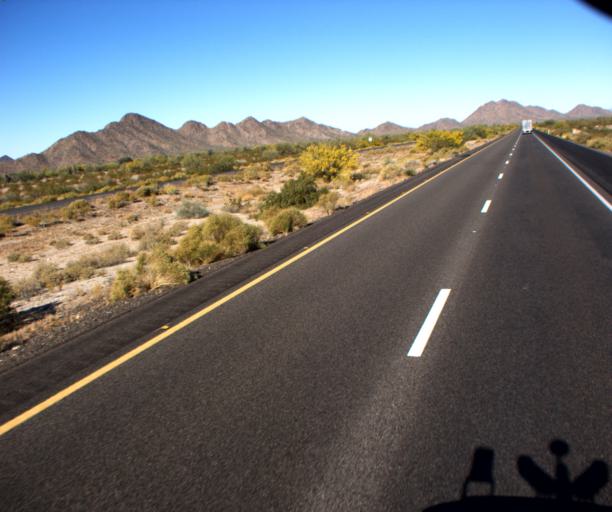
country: US
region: Arizona
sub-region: Maricopa County
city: Gila Bend
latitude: 32.8968
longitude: -112.5027
